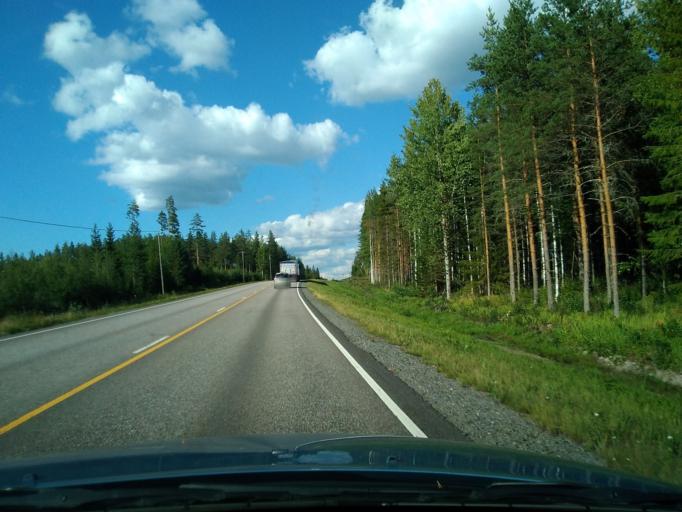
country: FI
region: Central Finland
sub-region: Keuruu
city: Keuruu
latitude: 62.1328
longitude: 24.7372
